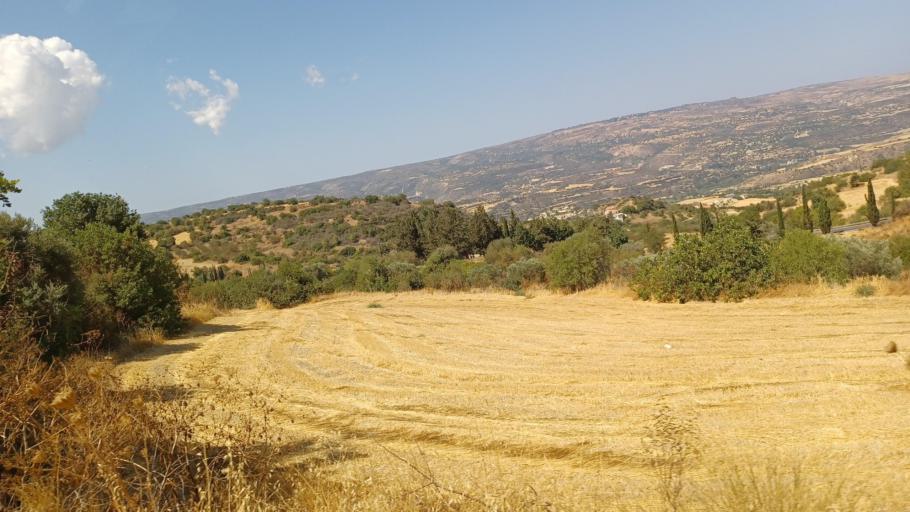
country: CY
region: Pafos
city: Polis
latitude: 34.9868
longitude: 32.4909
